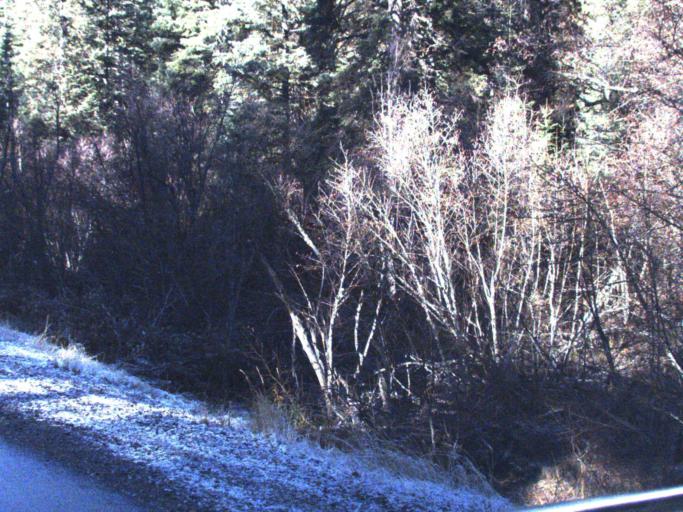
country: US
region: Washington
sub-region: Asotin County
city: Asotin
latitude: 46.0871
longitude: -117.1708
